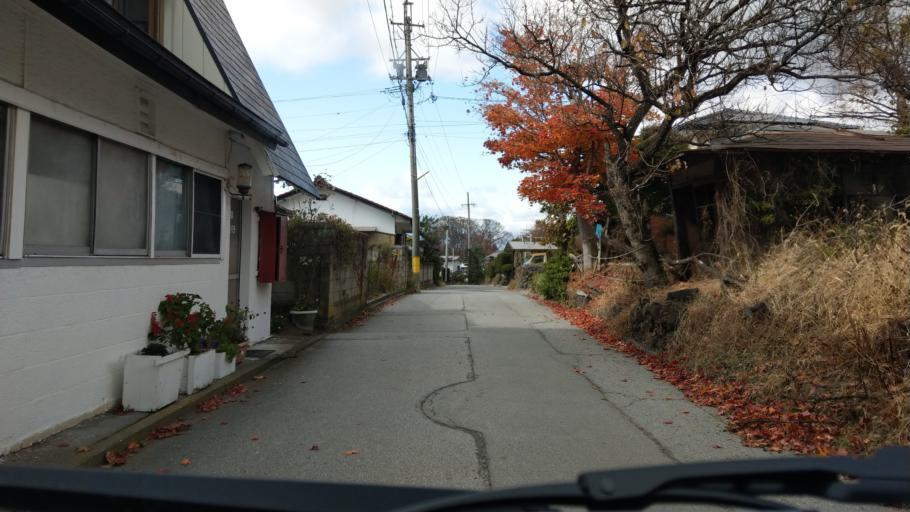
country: JP
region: Nagano
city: Komoro
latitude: 36.3217
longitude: 138.4965
